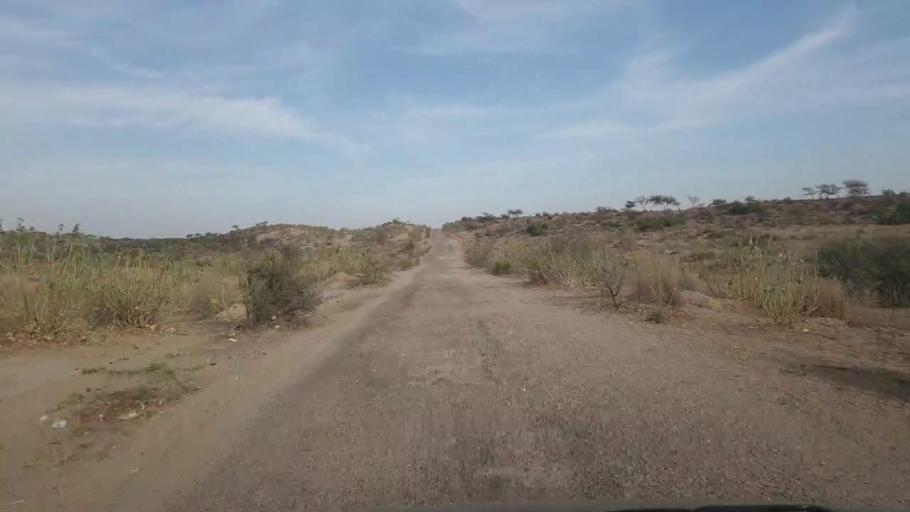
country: PK
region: Sindh
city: Nabisar
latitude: 25.0533
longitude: 69.6891
